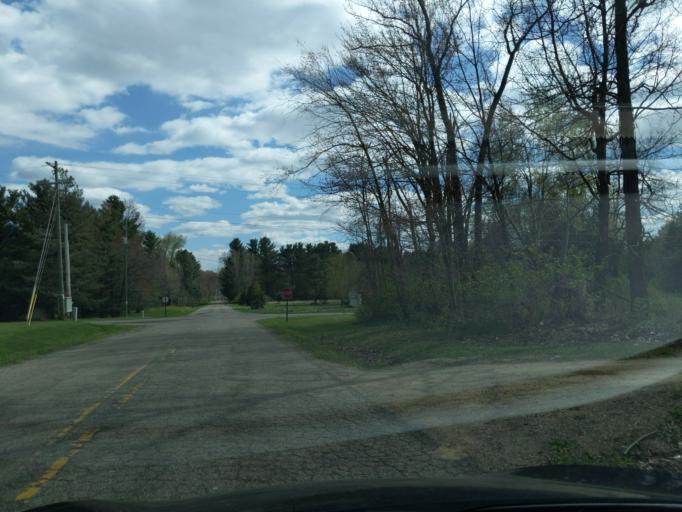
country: US
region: Michigan
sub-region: Ingham County
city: Leslie
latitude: 42.4086
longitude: -84.5269
